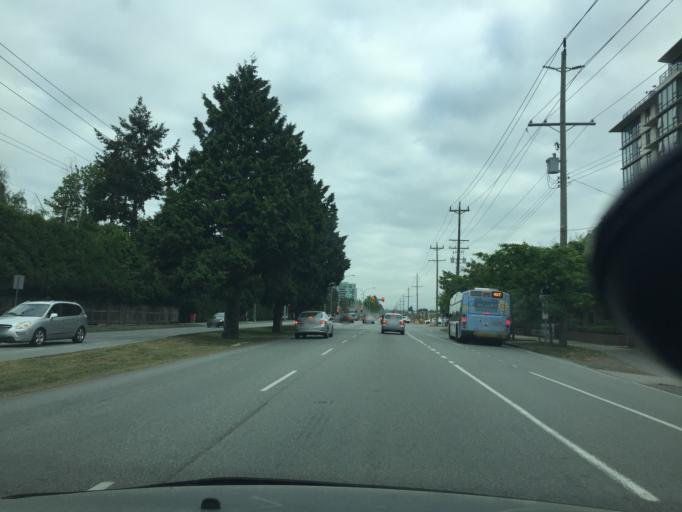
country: CA
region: British Columbia
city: Richmond
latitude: 49.1688
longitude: -123.1245
